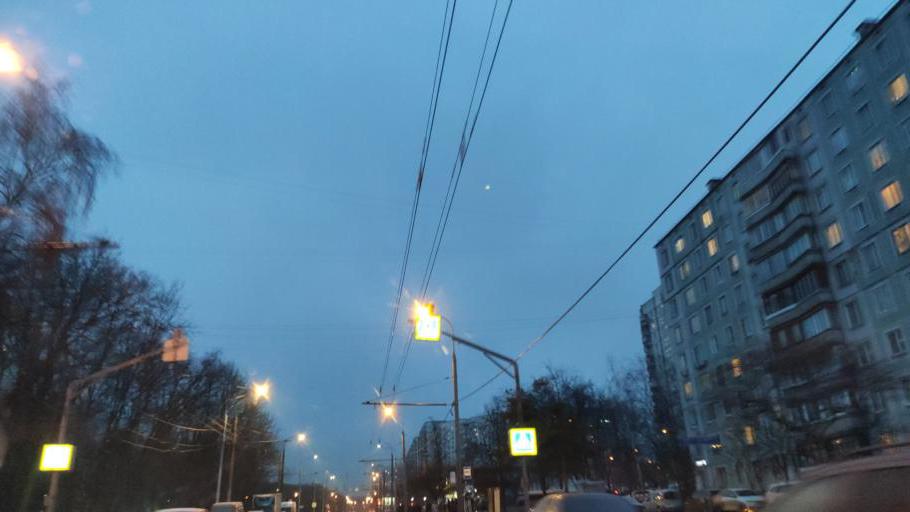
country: RU
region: Moscow
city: Yasenevo
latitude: 55.6053
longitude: 37.5234
